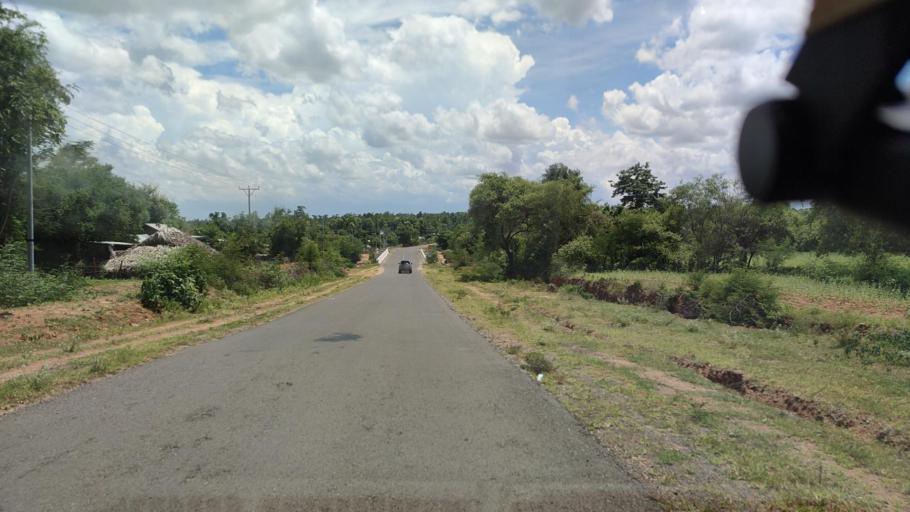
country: MM
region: Magway
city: Magway
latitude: 20.1912
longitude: 95.1457
